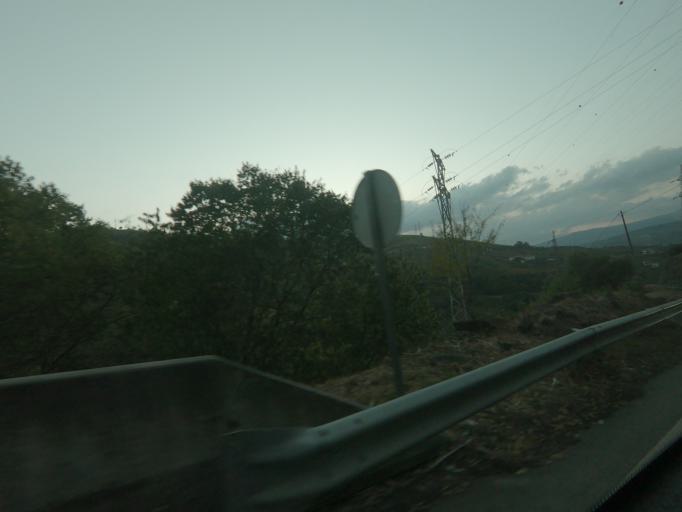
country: PT
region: Vila Real
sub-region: Peso da Regua
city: Peso da Regua
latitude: 41.1428
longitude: -7.7745
